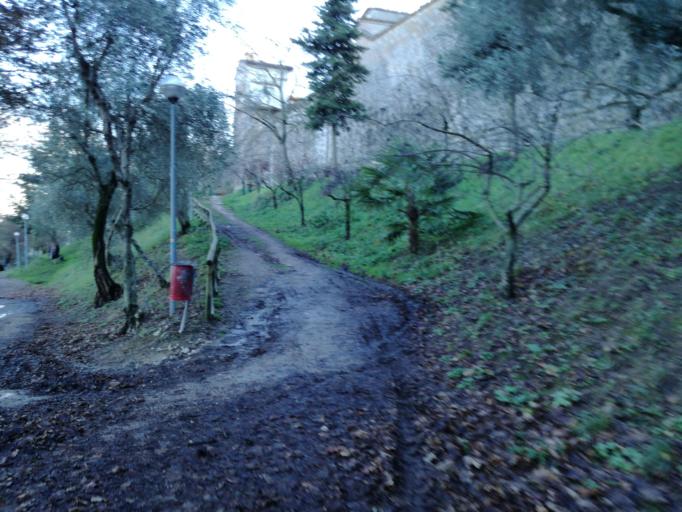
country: IT
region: Umbria
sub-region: Provincia di Perugia
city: Perugia
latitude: 43.1185
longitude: 12.3878
